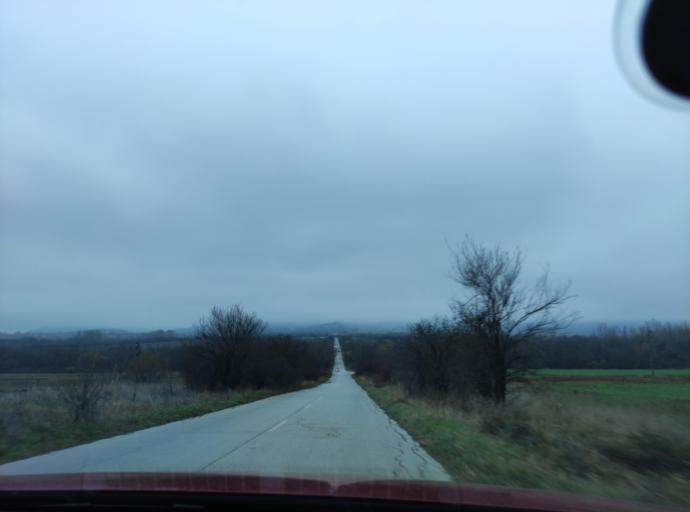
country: BG
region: Lovech
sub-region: Obshtina Yablanitsa
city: Yablanitsa
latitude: 43.0858
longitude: 24.0788
